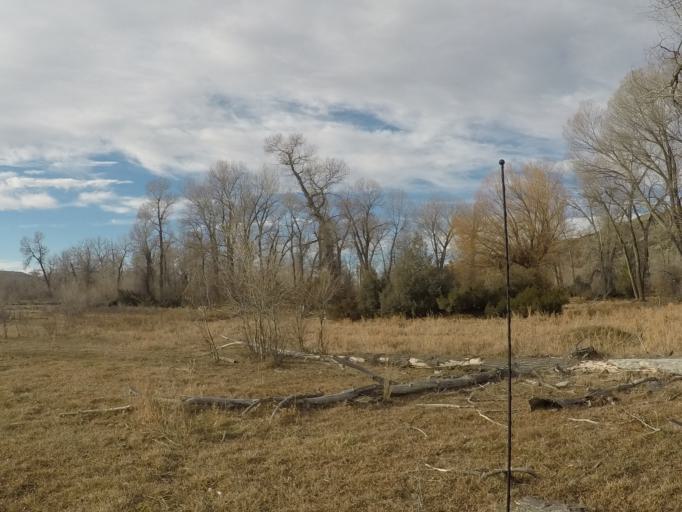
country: US
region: Montana
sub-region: Stillwater County
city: Absarokee
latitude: 45.5638
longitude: -109.3548
